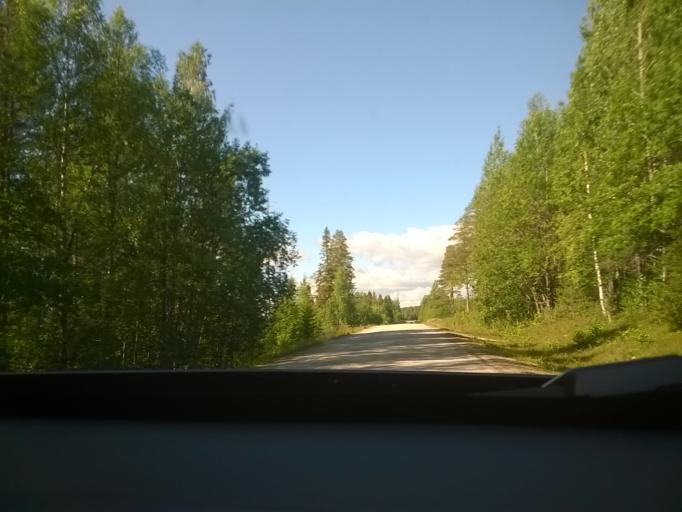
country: FI
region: Kainuu
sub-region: Kehys-Kainuu
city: Kuhmo
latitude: 64.4606
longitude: 29.6211
